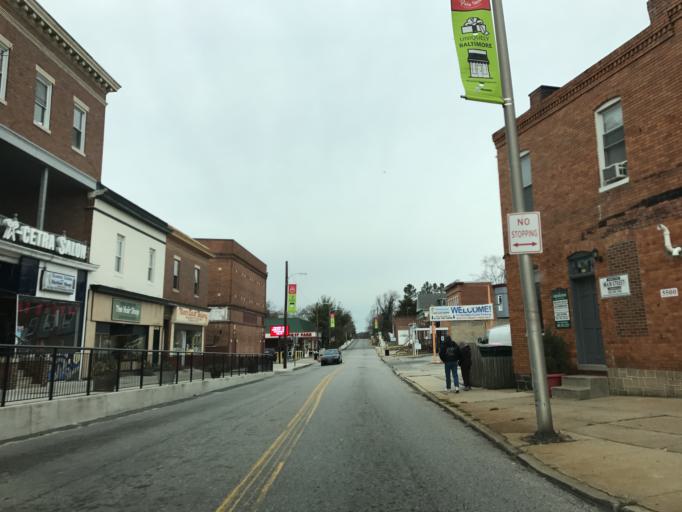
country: US
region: Maryland
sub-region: Baltimore County
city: Parkville
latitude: 39.3523
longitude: -76.5617
